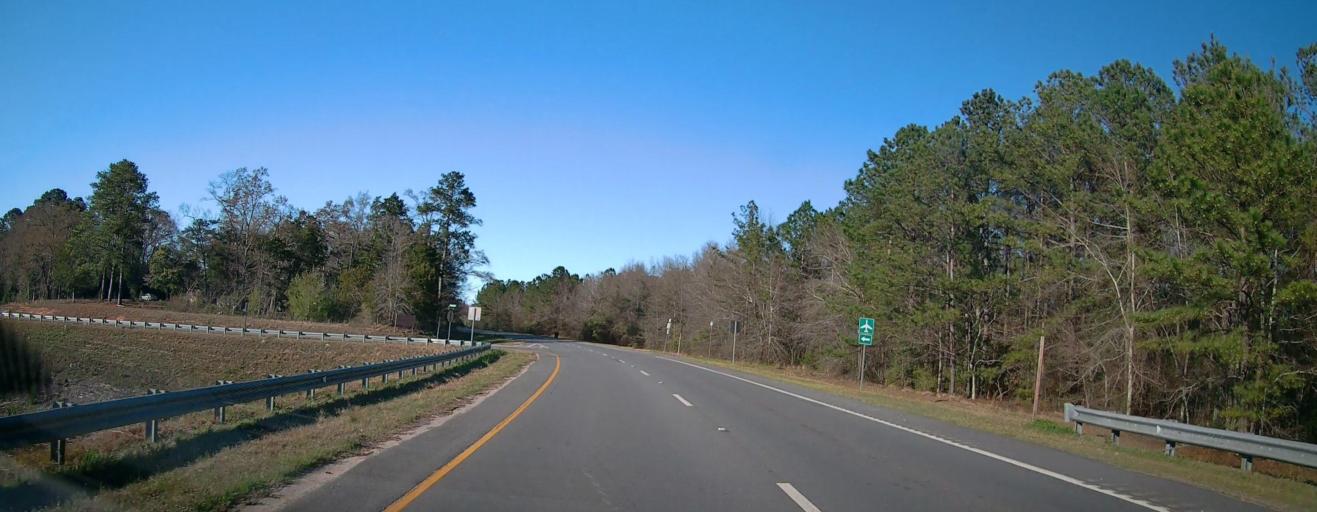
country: US
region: Georgia
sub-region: Taylor County
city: Butler
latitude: 32.5594
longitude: -84.2373
